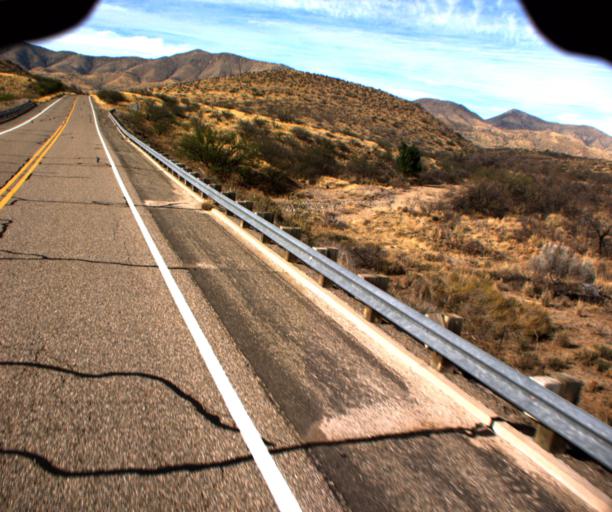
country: US
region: Arizona
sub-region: Cochise County
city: Willcox
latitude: 32.1453
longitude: -109.5650
